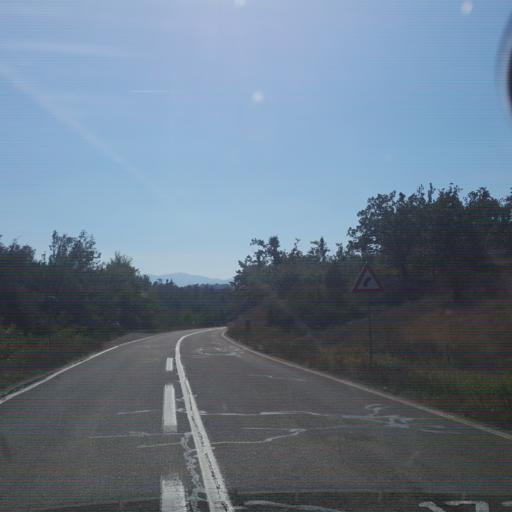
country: RS
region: Central Serbia
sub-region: Nisavski Okrug
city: Svrljig
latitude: 43.4612
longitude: 22.2087
